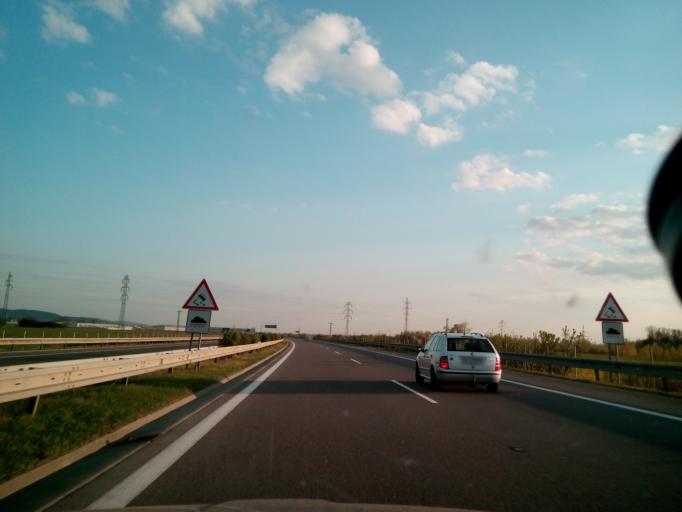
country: SK
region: Trenciansky
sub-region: Okres Nove Mesto nad Vahom
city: Nove Mesto nad Vahom
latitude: 48.7784
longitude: 17.8783
